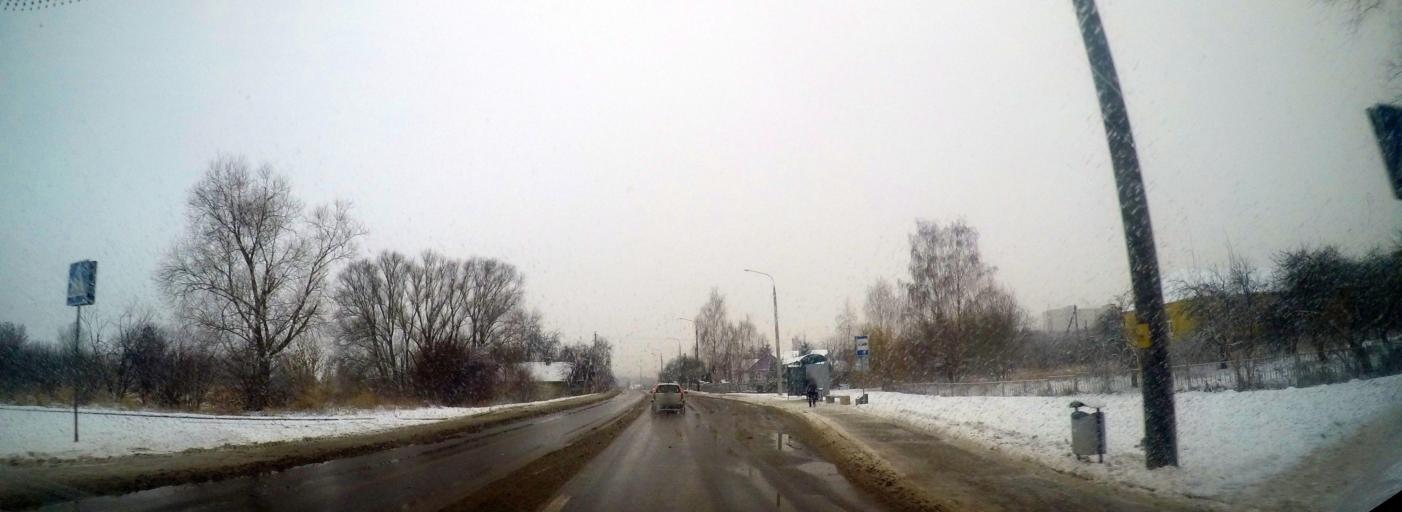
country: BY
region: Grodnenskaya
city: Hrodna
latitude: 53.7004
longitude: 23.8586
